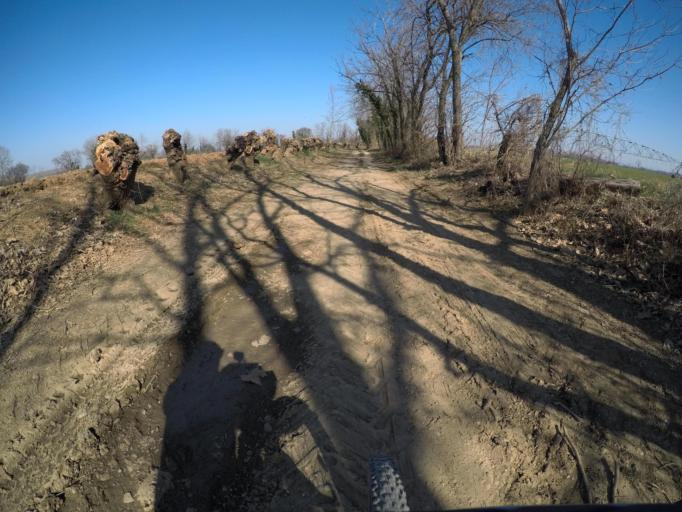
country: IT
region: Friuli Venezia Giulia
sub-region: Provincia di Udine
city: Lestizza
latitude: 45.9770
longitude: 13.1609
